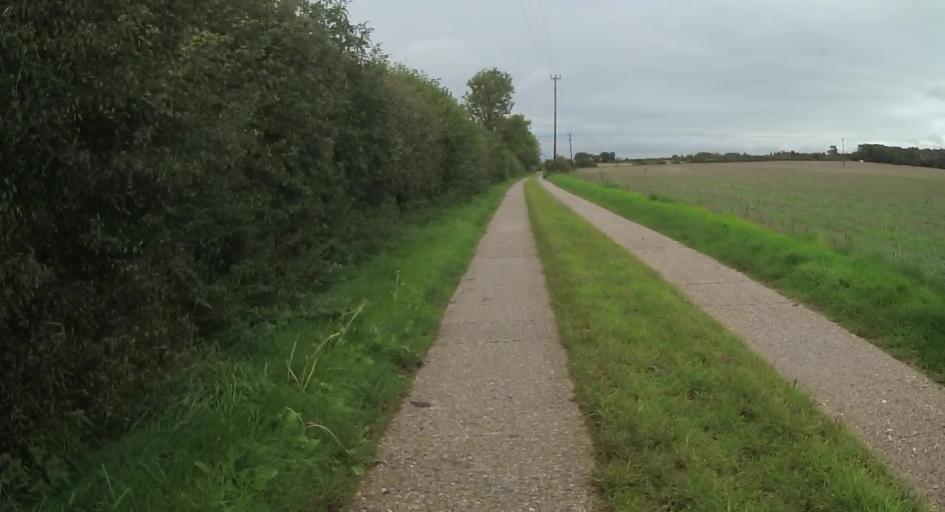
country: GB
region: England
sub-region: Hampshire
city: Basingstoke
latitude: 51.2742
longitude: -1.1357
